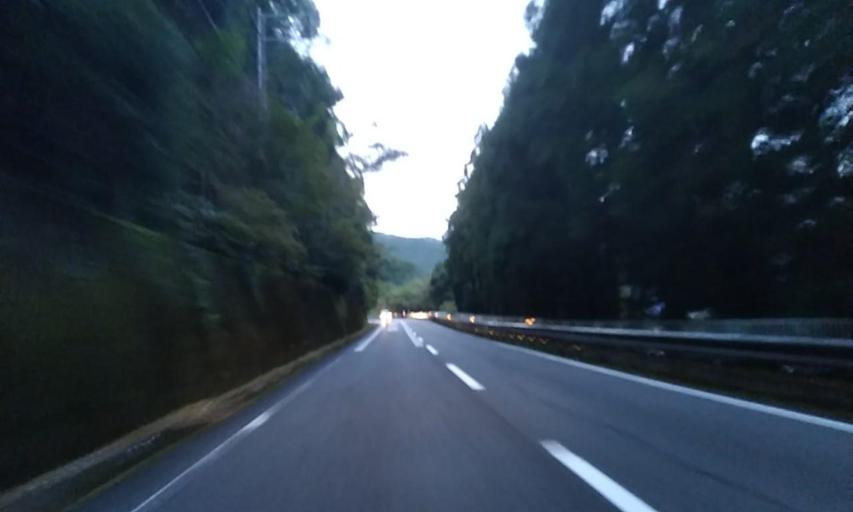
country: JP
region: Wakayama
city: Shingu
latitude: 33.7339
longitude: 135.9419
